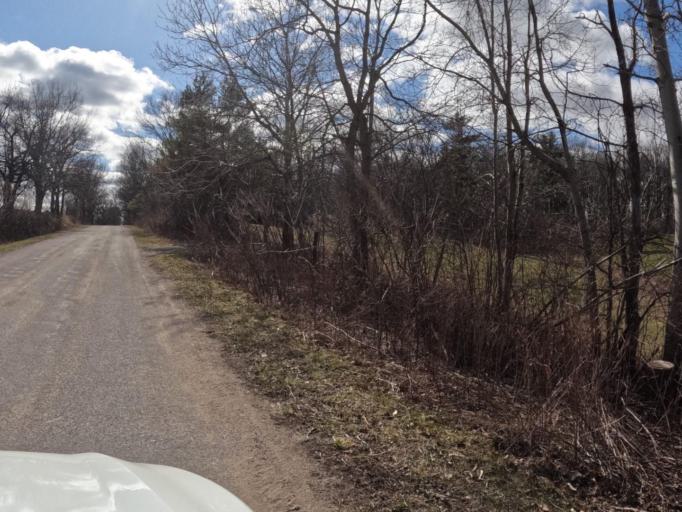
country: CA
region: Ontario
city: Norfolk County
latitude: 42.7488
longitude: -80.2911
